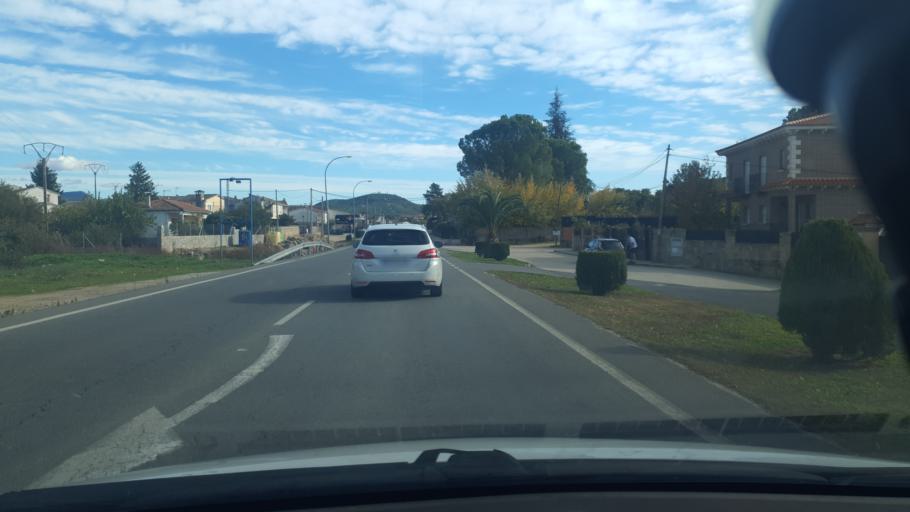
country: ES
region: Castille and Leon
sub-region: Provincia de Avila
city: La Adrada
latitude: 40.3051
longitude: -4.6449
